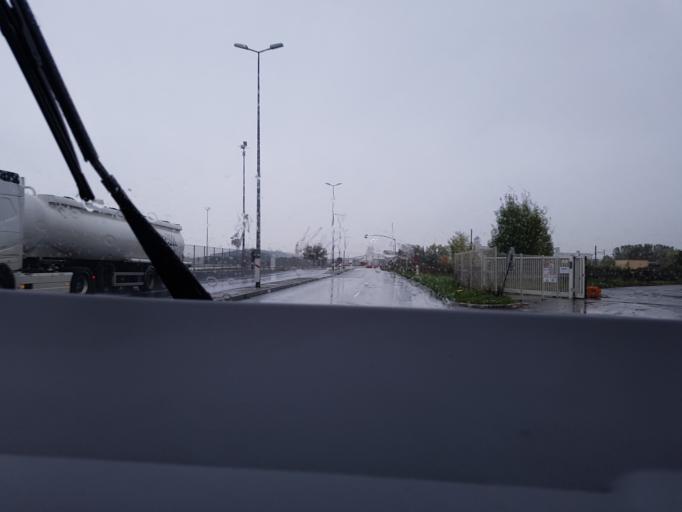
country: FR
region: Aquitaine
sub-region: Departement de la Gironde
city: Bassens
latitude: 44.9016
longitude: -0.5333
